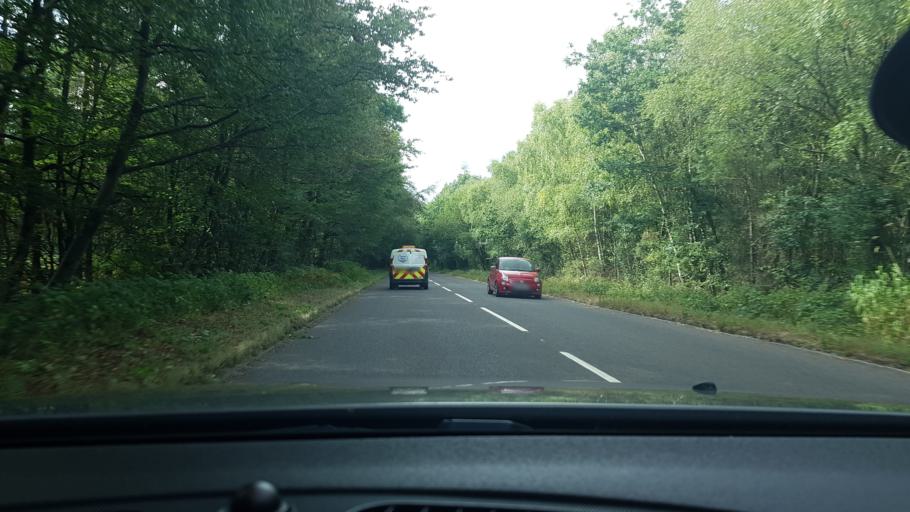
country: GB
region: England
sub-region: West Berkshire
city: Welford
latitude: 51.4278
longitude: -1.4043
